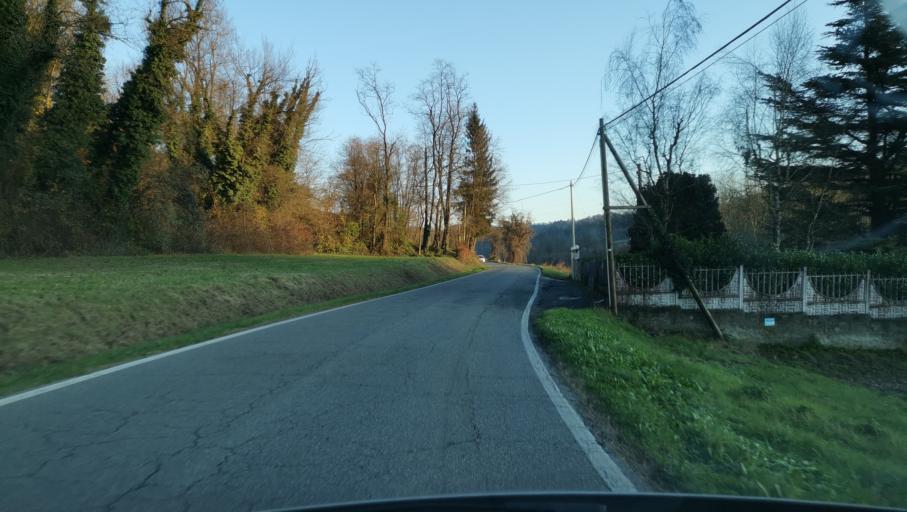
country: IT
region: Piedmont
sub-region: Provincia di Torino
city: Rivalba
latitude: 45.1153
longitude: 7.8724
